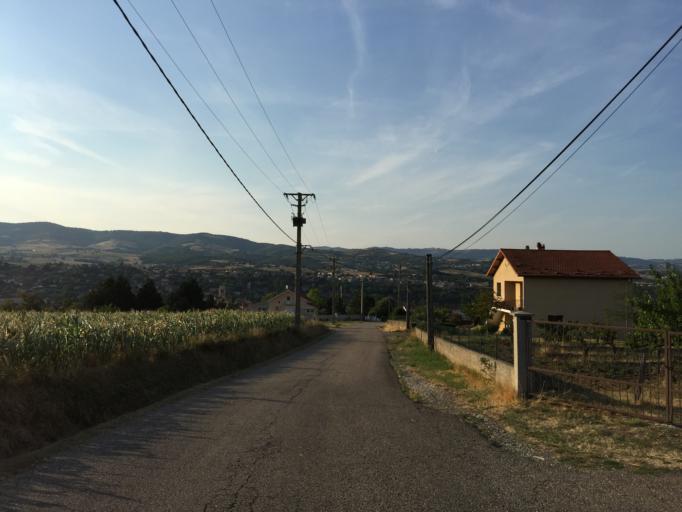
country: FR
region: Rhone-Alpes
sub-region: Departement de la Loire
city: La Grand-Croix
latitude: 45.4796
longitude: 4.5490
